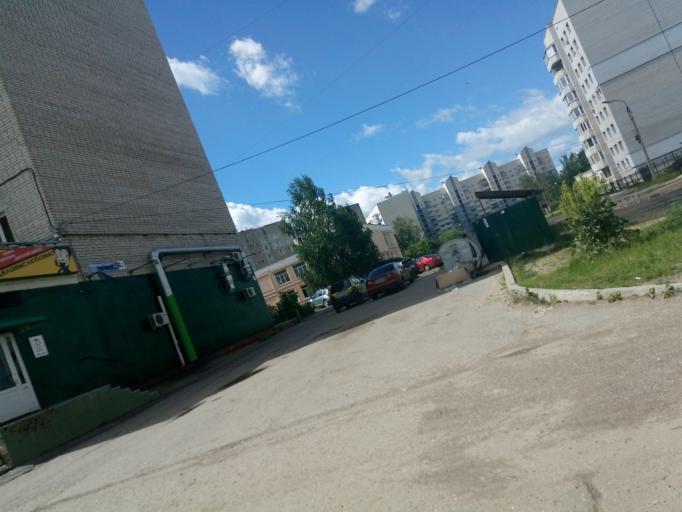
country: RU
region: Jaroslavl
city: Yaroslavl
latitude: 57.6404
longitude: 39.9606
